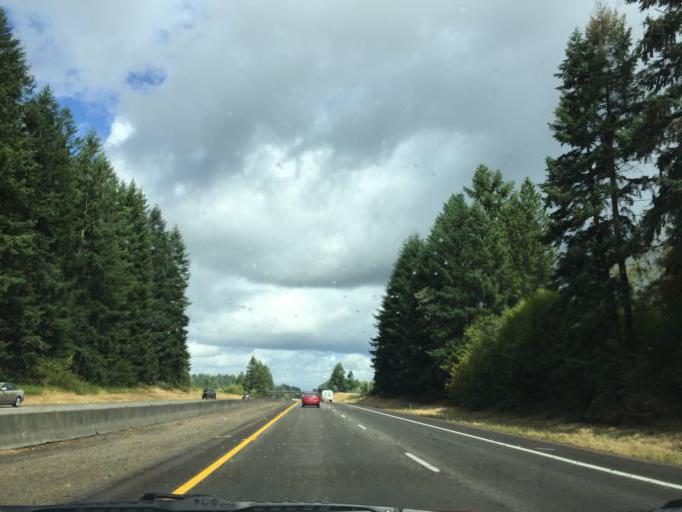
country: US
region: Washington
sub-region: Lewis County
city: Winlock
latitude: 46.5137
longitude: -122.8766
